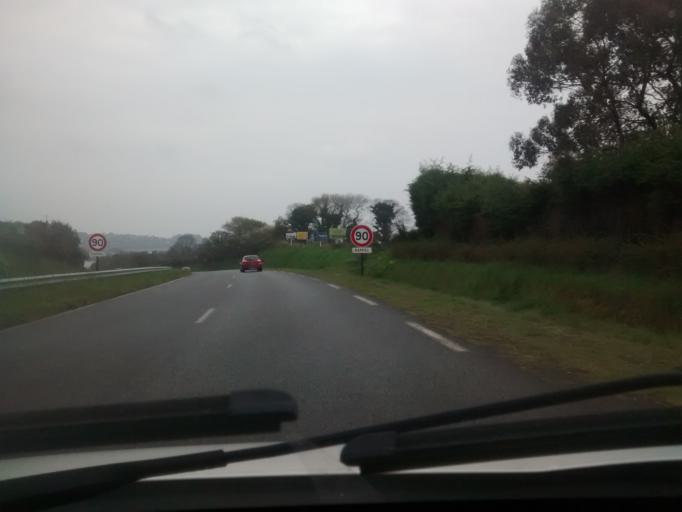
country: FR
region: Brittany
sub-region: Departement des Cotes-d'Armor
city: Saint-Quay-Perros
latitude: 48.7900
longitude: -3.4426
